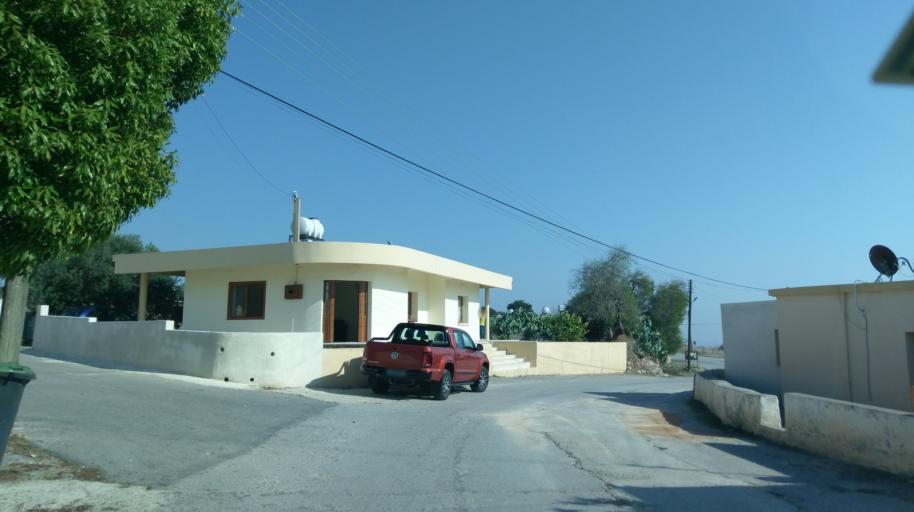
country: CY
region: Ammochostos
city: Leonarisso
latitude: 35.4906
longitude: 34.2187
